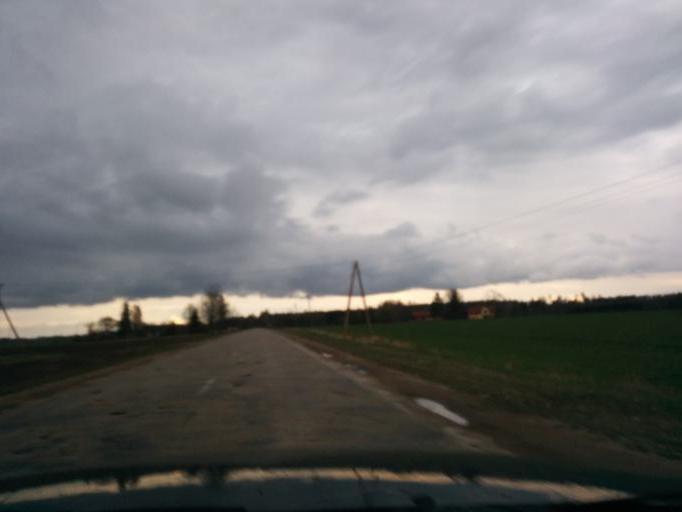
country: LT
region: Siauliu apskritis
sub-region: Joniskis
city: Joniskis
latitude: 56.4183
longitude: 23.5710
